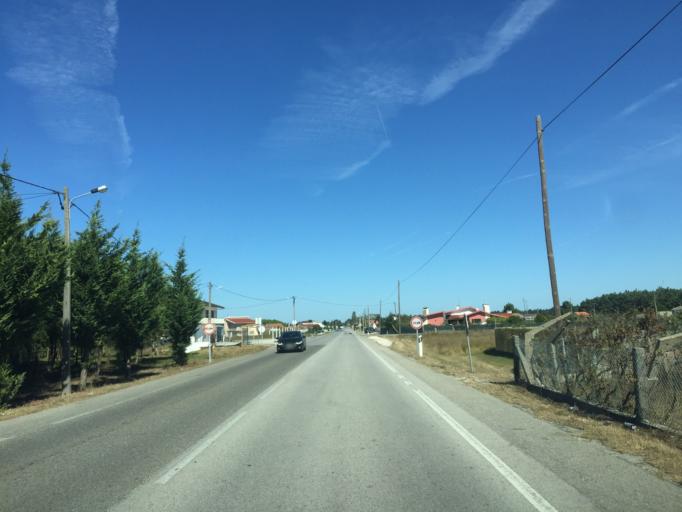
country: PT
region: Coimbra
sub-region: Figueira da Foz
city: Alhadas
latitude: 40.2290
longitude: -8.8013
